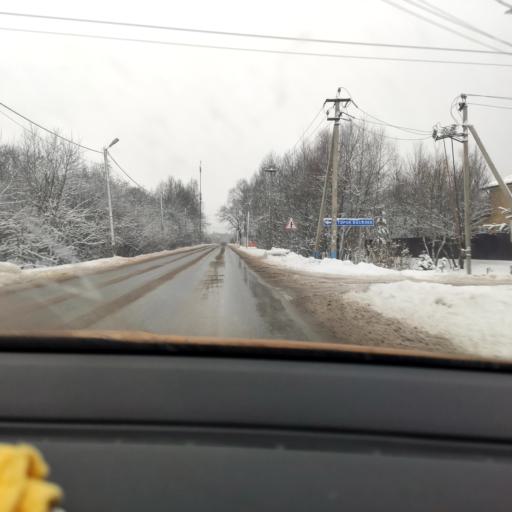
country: RU
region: Moskovskaya
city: Yershovo
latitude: 55.7543
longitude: 36.8702
